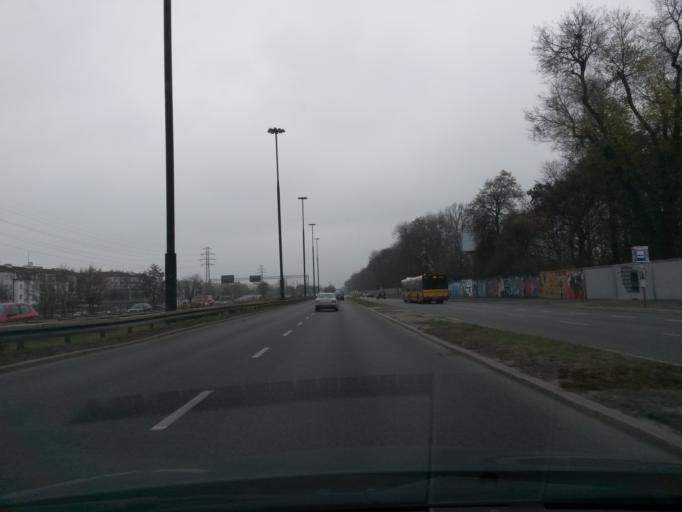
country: PL
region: Masovian Voivodeship
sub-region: Warszawa
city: Mokotow
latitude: 52.1647
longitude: 21.0171
